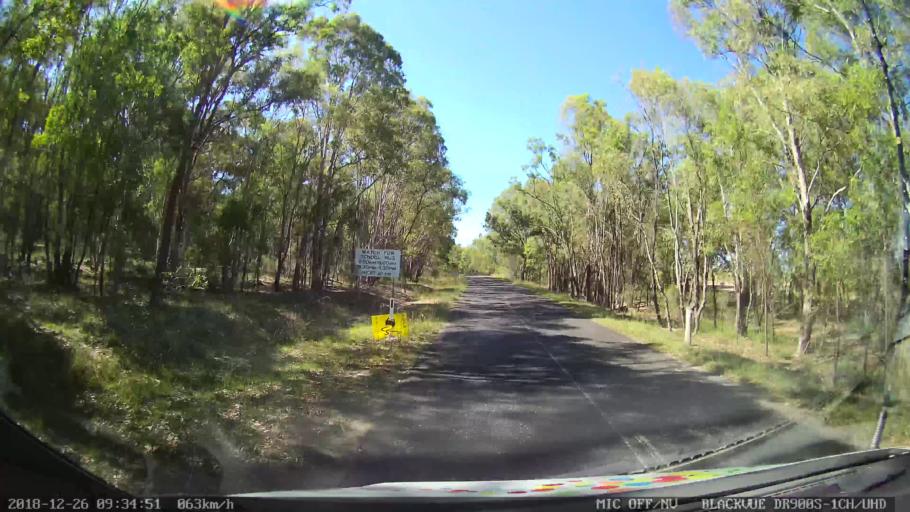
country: AU
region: New South Wales
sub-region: Mid-Western Regional
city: Kandos
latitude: -32.9095
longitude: 150.0382
